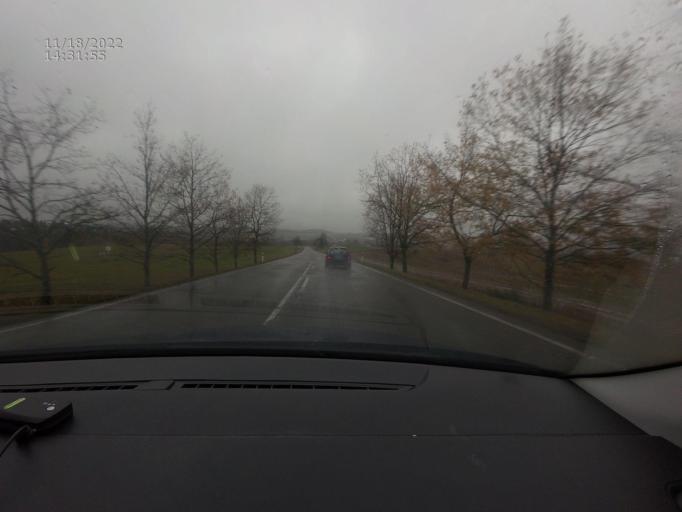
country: CZ
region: Jihocesky
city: Kovarov
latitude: 49.4510
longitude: 14.2700
